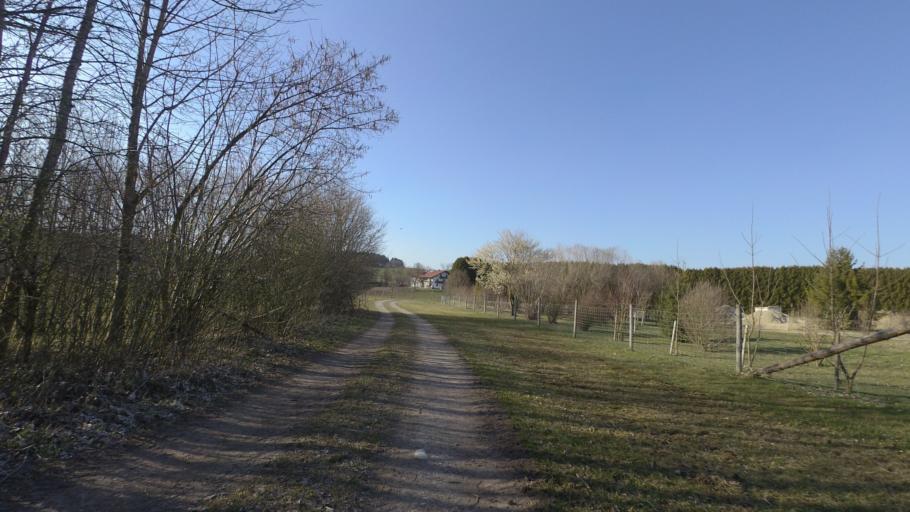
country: DE
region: Bavaria
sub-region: Upper Bavaria
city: Chieming
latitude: 47.9407
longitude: 12.5468
